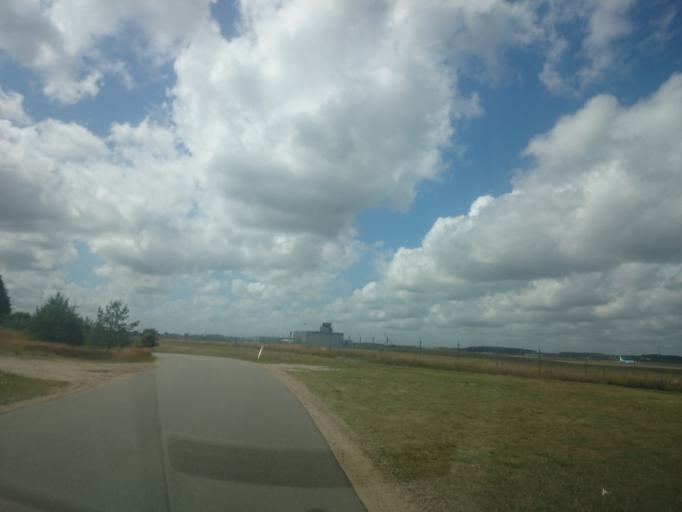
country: DK
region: South Denmark
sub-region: Billund Kommune
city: Billund
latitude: 55.7372
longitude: 9.1733
